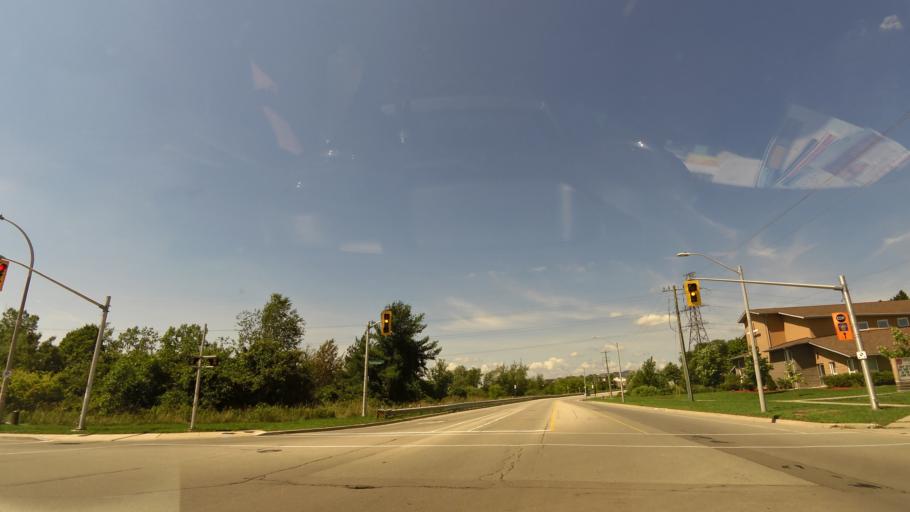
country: CA
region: Ontario
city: Ancaster
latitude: 43.2242
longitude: -79.9343
